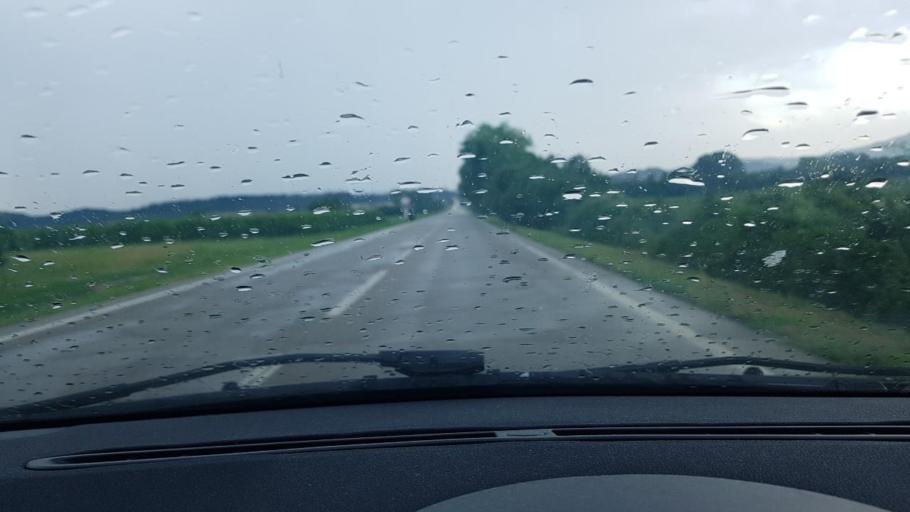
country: IT
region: Veneto
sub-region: Provincia di Verona
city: Caprino Veronese
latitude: 45.5953
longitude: 10.7693
